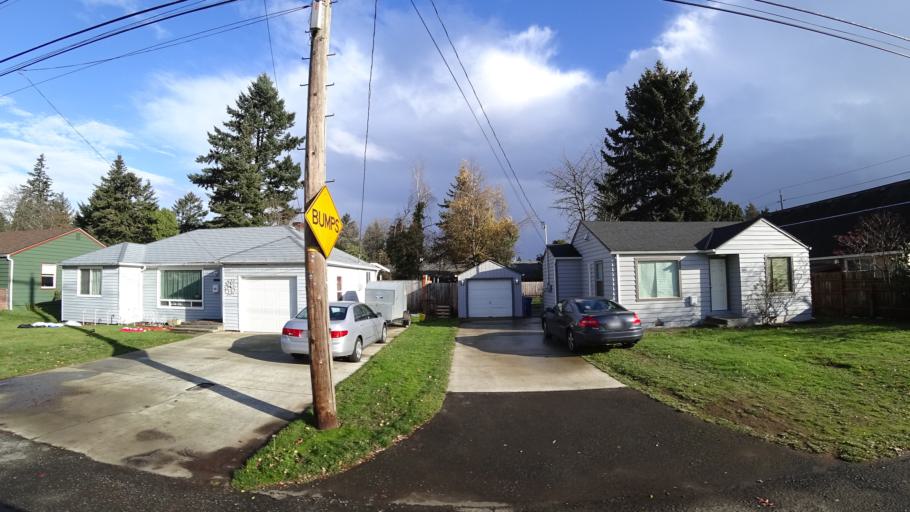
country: US
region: Oregon
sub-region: Multnomah County
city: Lents
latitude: 45.5269
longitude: -122.5485
